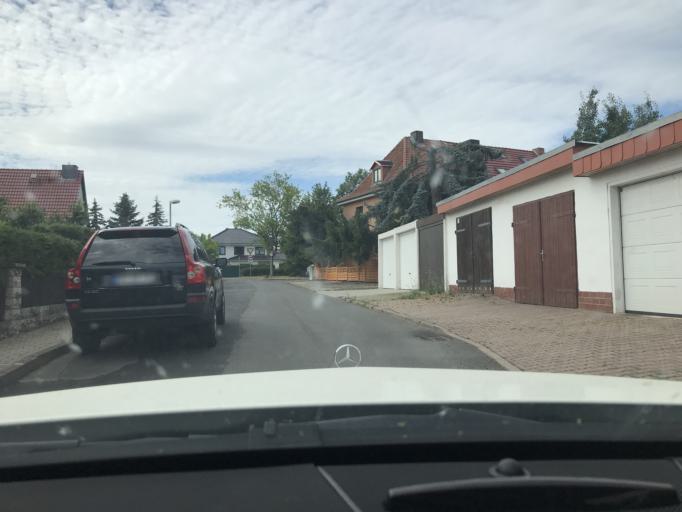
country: DE
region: Thuringia
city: Muehlhausen
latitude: 51.2023
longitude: 10.4746
